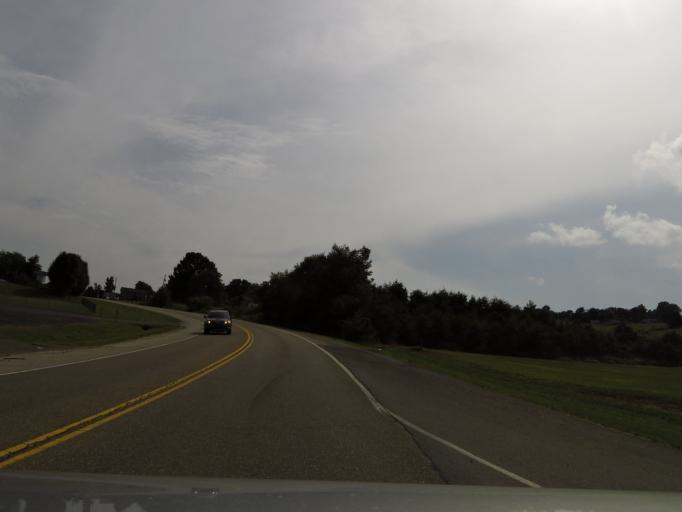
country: US
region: Tennessee
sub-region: Blount County
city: Alcoa
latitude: 35.8587
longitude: -83.9792
